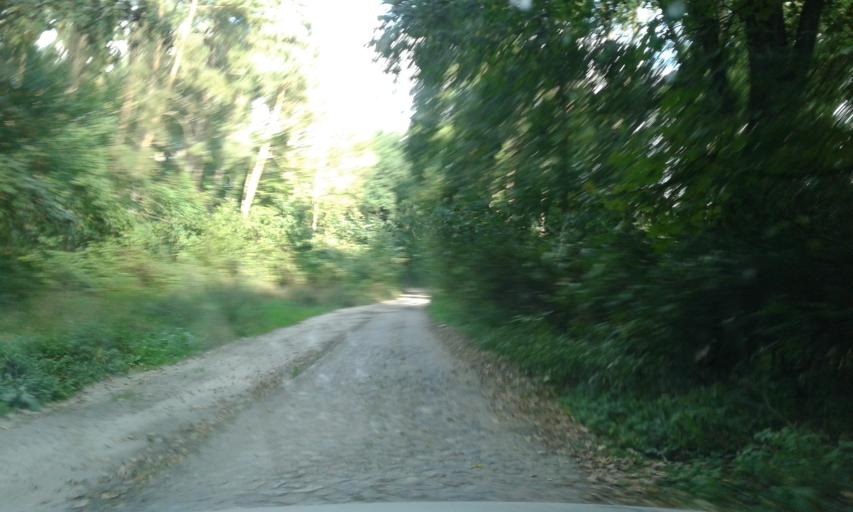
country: PL
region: West Pomeranian Voivodeship
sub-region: Powiat stargardzki
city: Dolice
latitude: 53.2467
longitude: 15.2239
